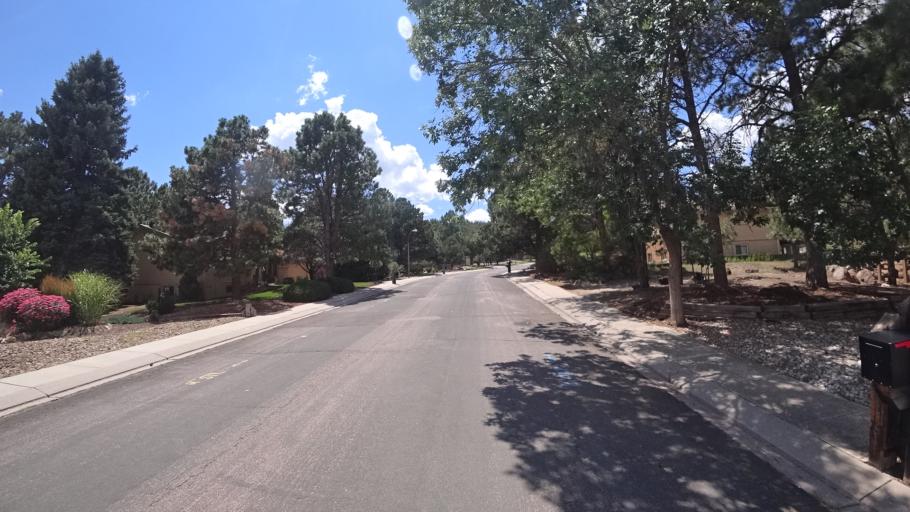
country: US
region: Colorado
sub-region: El Paso County
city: Air Force Academy
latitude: 38.9358
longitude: -104.8379
